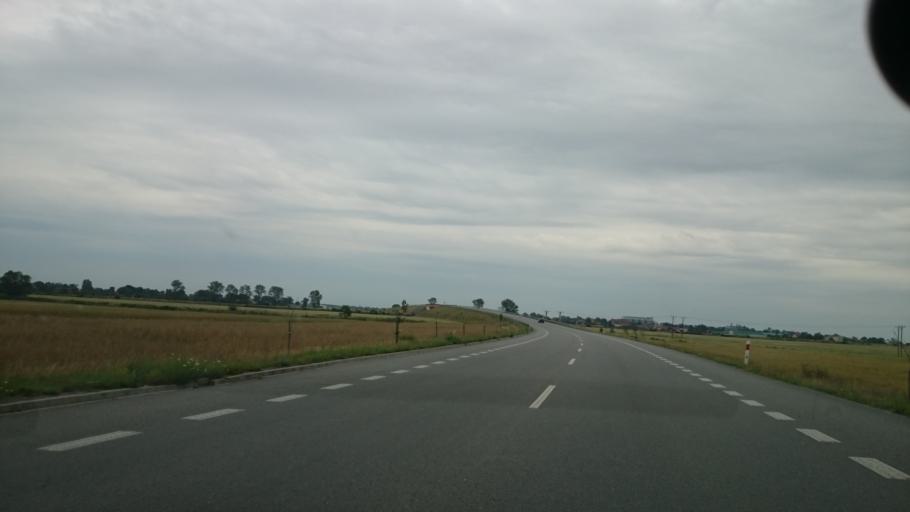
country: PL
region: Opole Voivodeship
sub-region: Powiat brzeski
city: Grodkow
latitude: 50.6858
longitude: 17.3699
